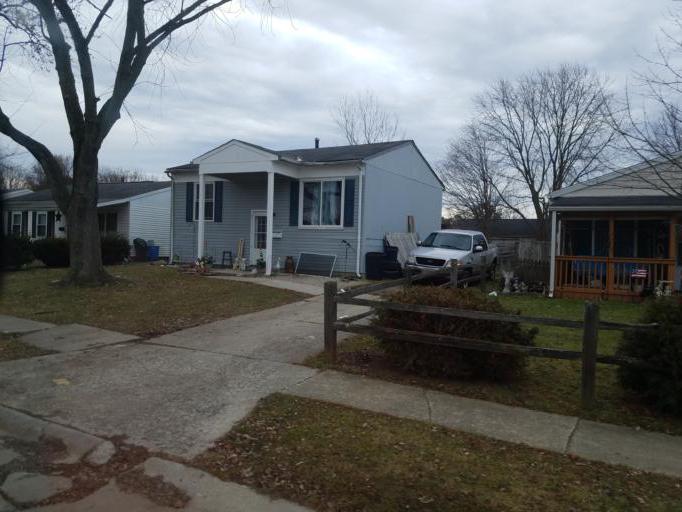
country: US
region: Ohio
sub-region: Marion County
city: Marion
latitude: 40.6088
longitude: -83.1142
